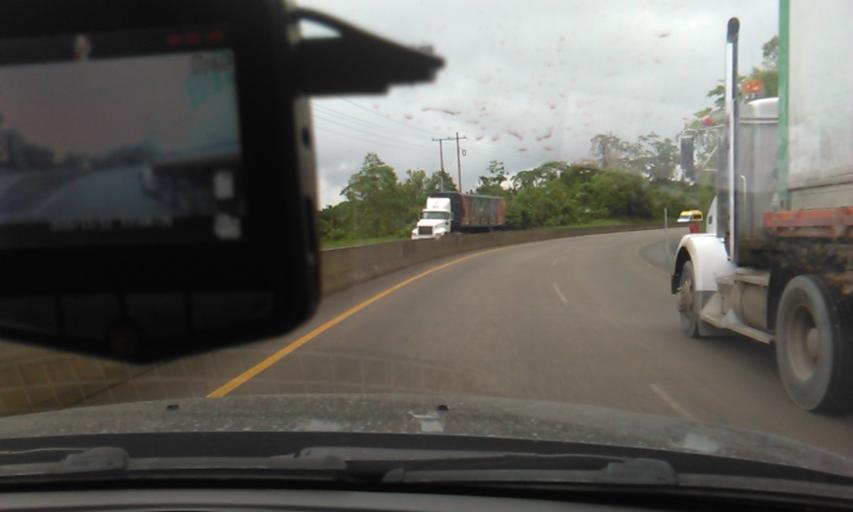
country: CO
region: Valle del Cauca
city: Buenaventura
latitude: 3.8789
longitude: -76.9117
